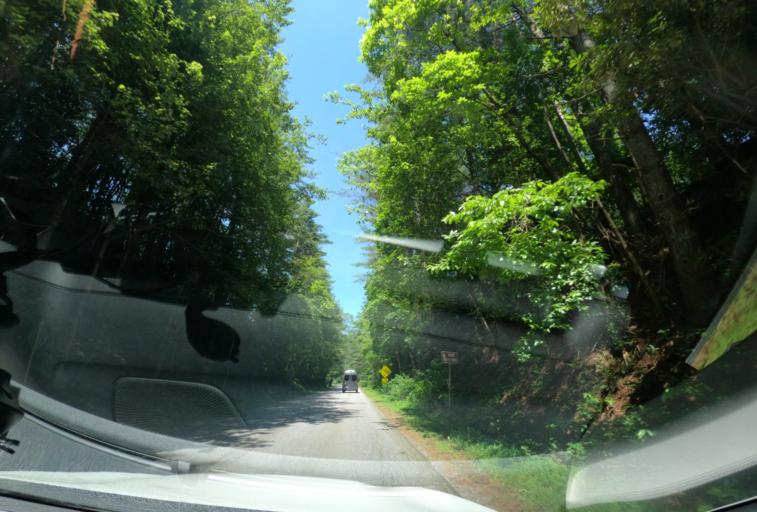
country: US
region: North Carolina
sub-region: Transylvania County
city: Brevard
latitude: 35.1494
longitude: -82.6455
